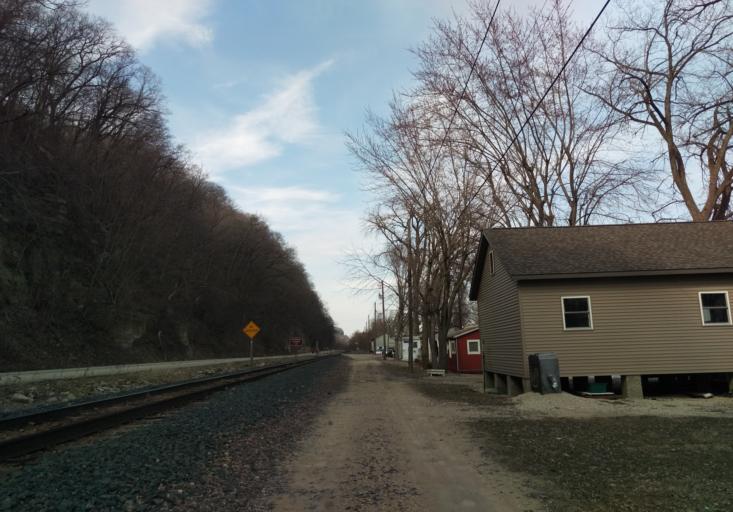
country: US
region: Wisconsin
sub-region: Crawford County
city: Prairie du Chien
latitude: 43.0712
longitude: -91.1802
